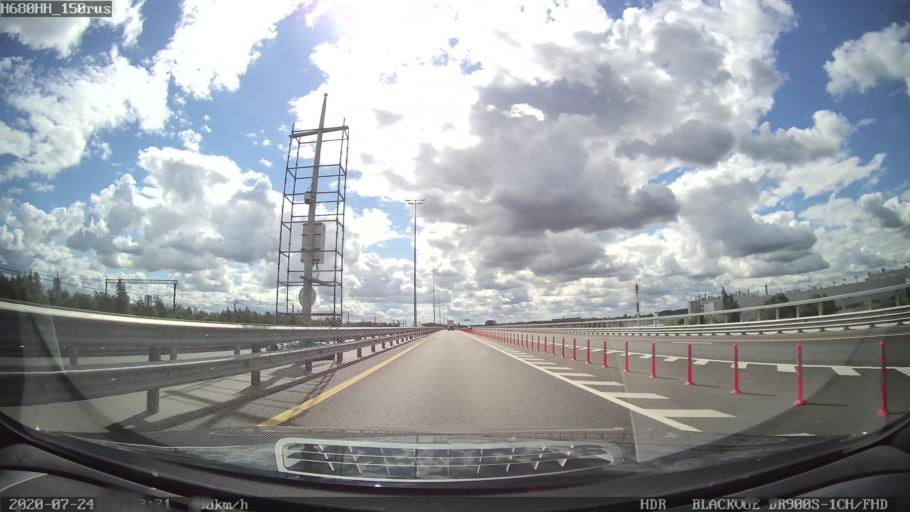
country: RU
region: St.-Petersburg
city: Shushary
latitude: 59.8042
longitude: 30.3357
